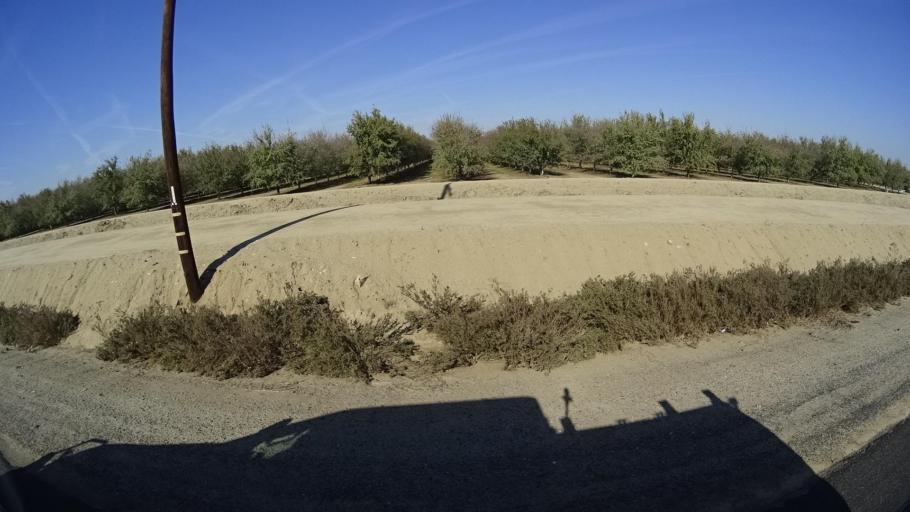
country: US
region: California
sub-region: Kern County
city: Wasco
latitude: 35.6452
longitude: -119.3044
